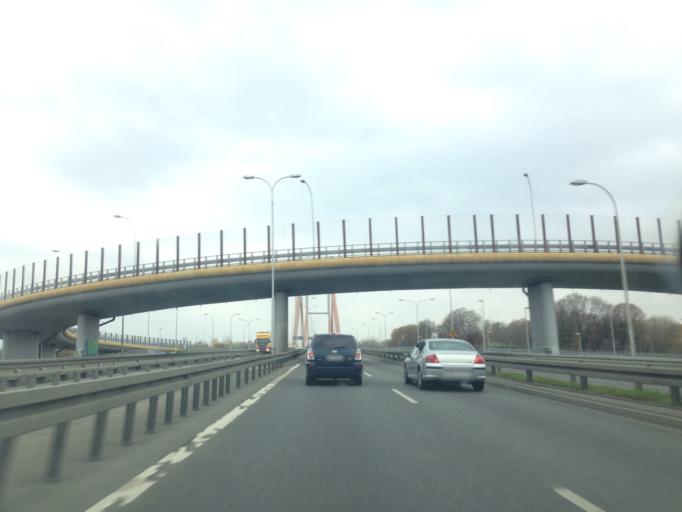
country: PL
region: Masovian Voivodeship
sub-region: Warszawa
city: Praga Poludnie
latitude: 52.2192
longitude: 21.0992
